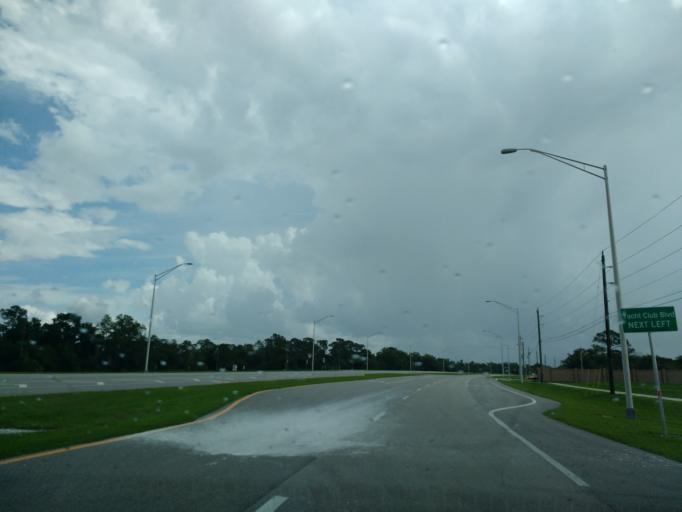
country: US
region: Florida
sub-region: Lee County
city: Burnt Store Marina
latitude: 26.7999
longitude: -82.0368
